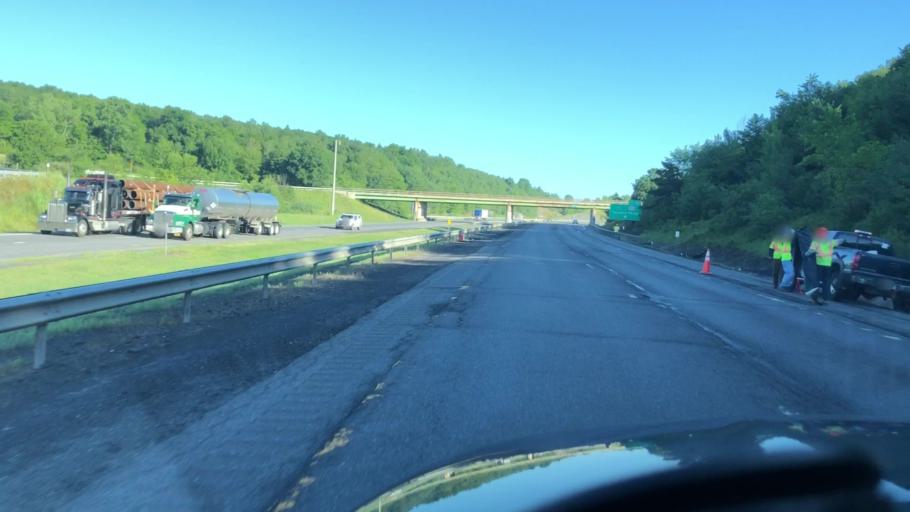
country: US
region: New York
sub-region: Columbia County
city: Chatham
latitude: 42.4189
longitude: -73.5468
